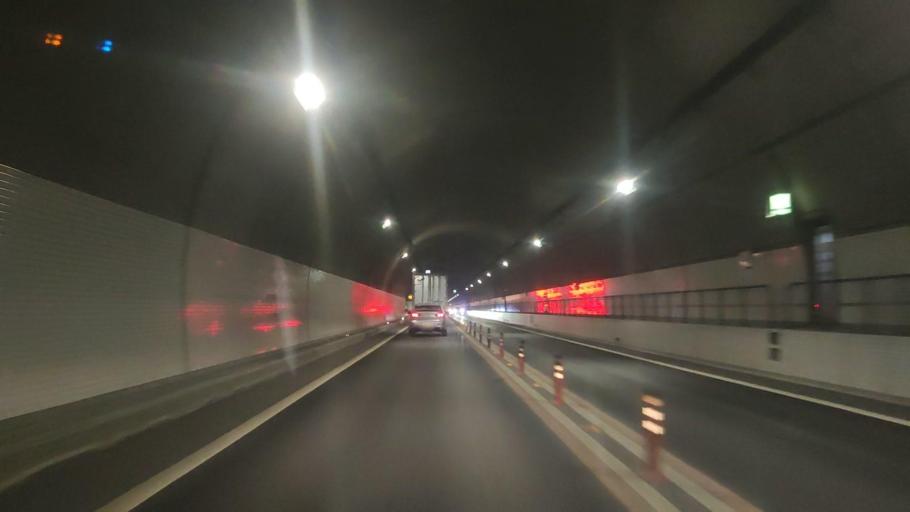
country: JP
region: Fukuoka
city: Kanda
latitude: 33.7589
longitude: 130.9597
